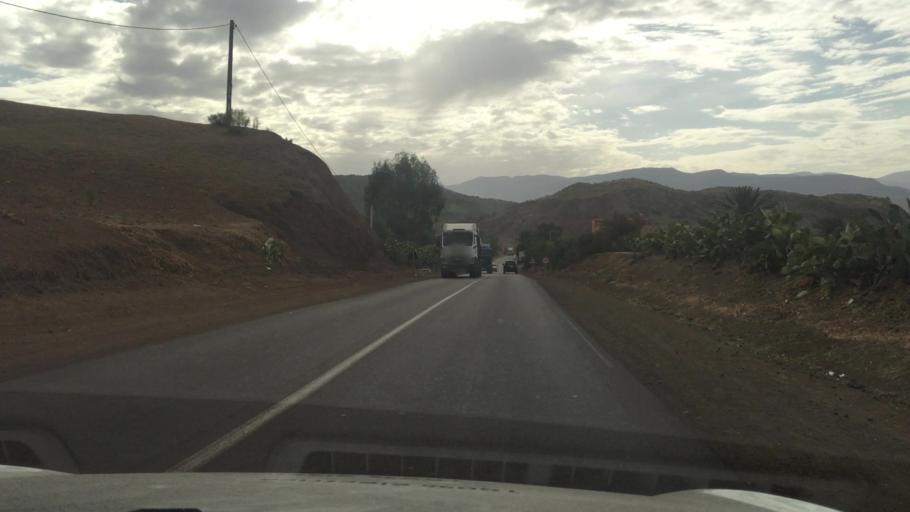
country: MA
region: Marrakech-Tensift-Al Haouz
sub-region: Al-Haouz
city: Touama
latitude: 31.5491
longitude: -7.5767
